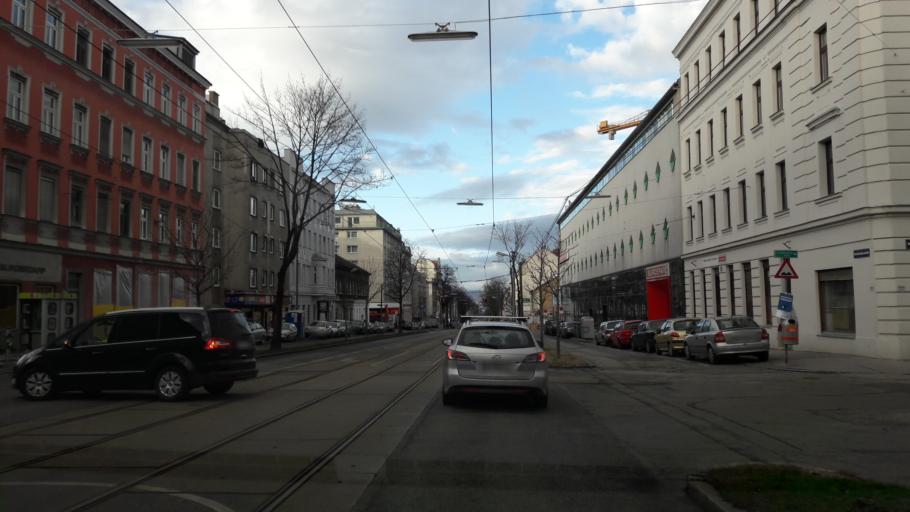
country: AT
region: Vienna
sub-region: Wien Stadt
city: Vienna
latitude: 48.1652
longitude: 16.3820
